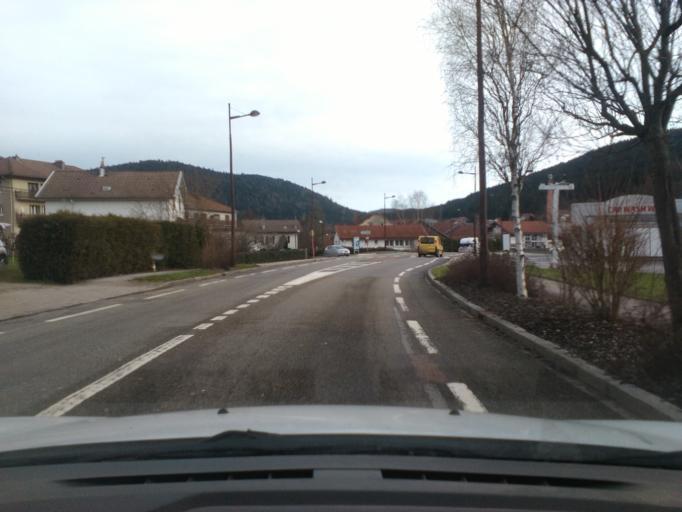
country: FR
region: Lorraine
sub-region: Departement des Vosges
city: Gerardmer
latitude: 48.0785
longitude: 6.8819
